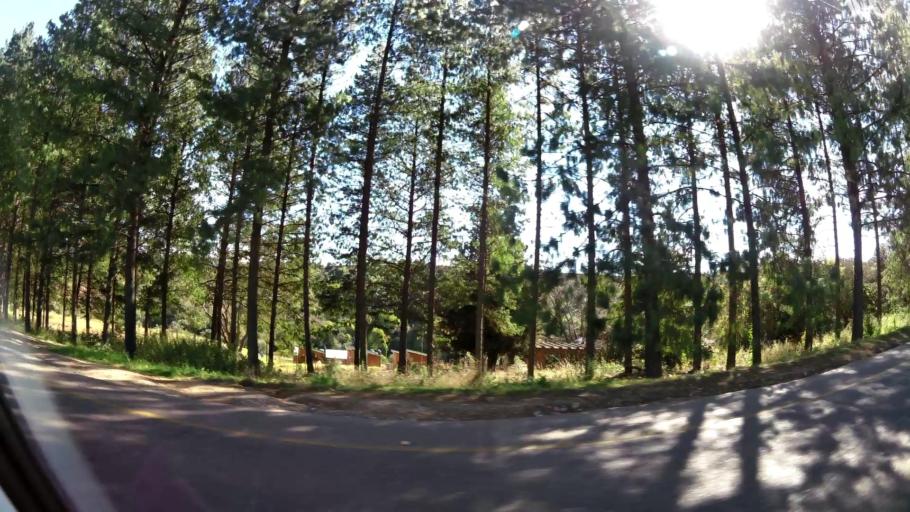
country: ZA
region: Limpopo
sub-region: Capricorn District Municipality
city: Mankoeng
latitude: -23.9331
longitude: 29.9558
